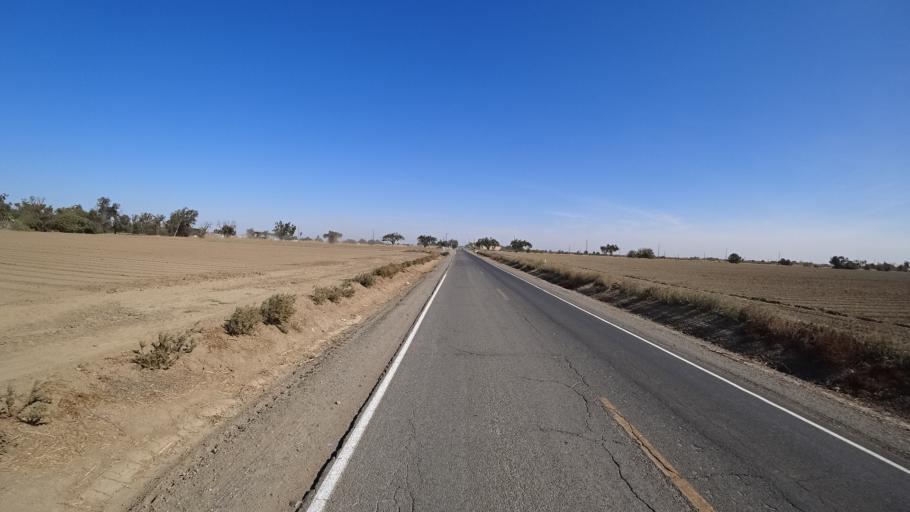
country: US
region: California
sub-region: Yolo County
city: Woodland
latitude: 38.6412
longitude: -121.7700
